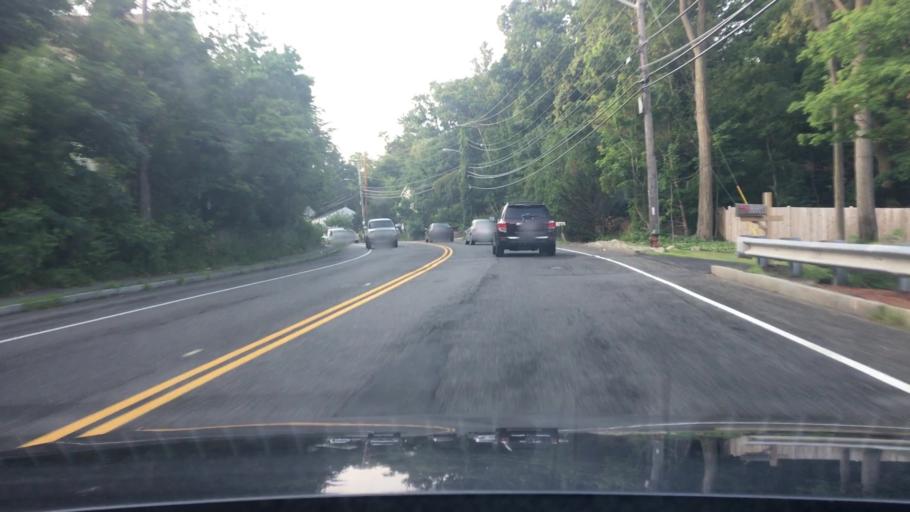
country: US
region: Massachusetts
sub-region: Essex County
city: Saugus
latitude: 42.4860
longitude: -71.0139
